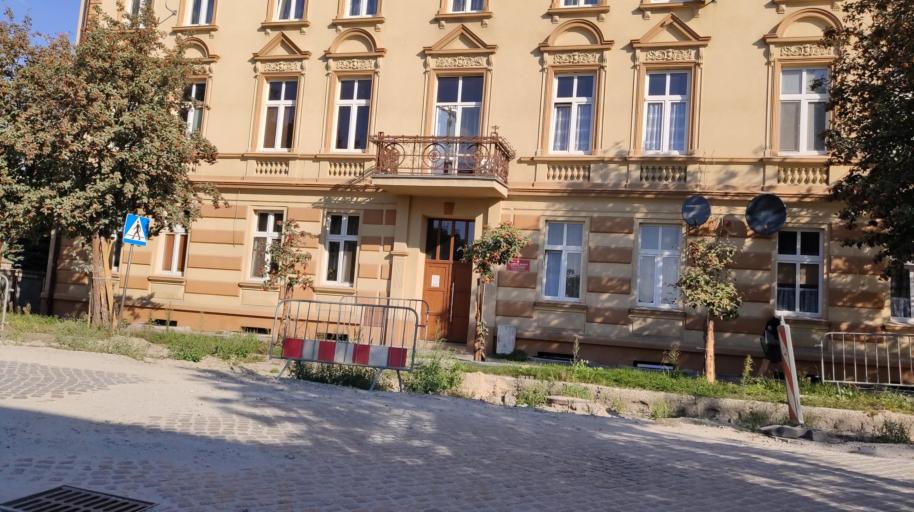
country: PL
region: Kujawsko-Pomorskie
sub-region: Powiat zninski
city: Znin
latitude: 52.8475
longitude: 17.7320
